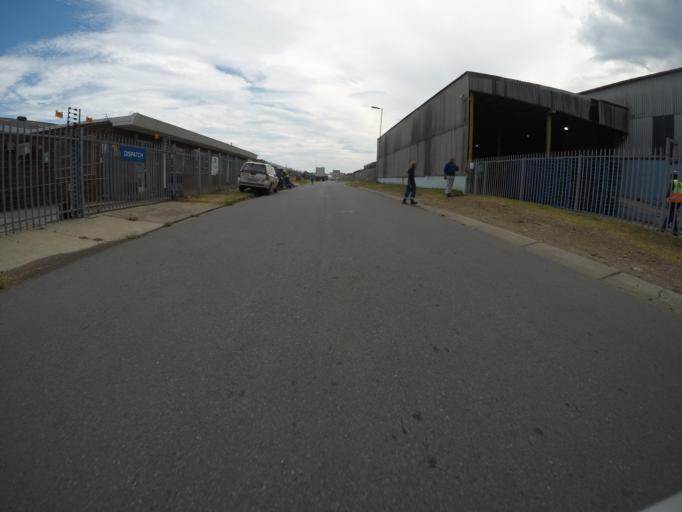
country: ZA
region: Eastern Cape
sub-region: Buffalo City Metropolitan Municipality
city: East London
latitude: -33.0280
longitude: 27.8871
